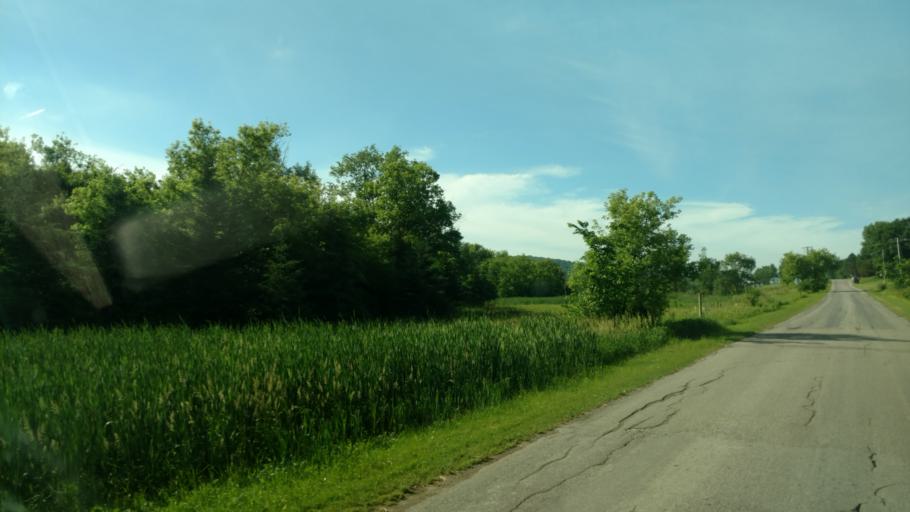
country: US
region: Wisconsin
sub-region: Sauk County
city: Reedsburg
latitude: 43.5514
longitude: -90.1389
